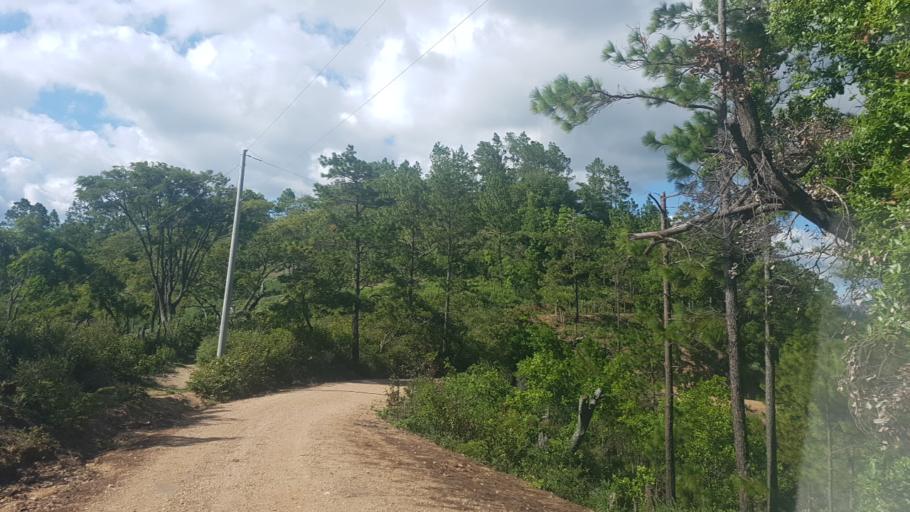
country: HN
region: Choluteca
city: Duyure
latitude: 13.6420
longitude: -86.6530
